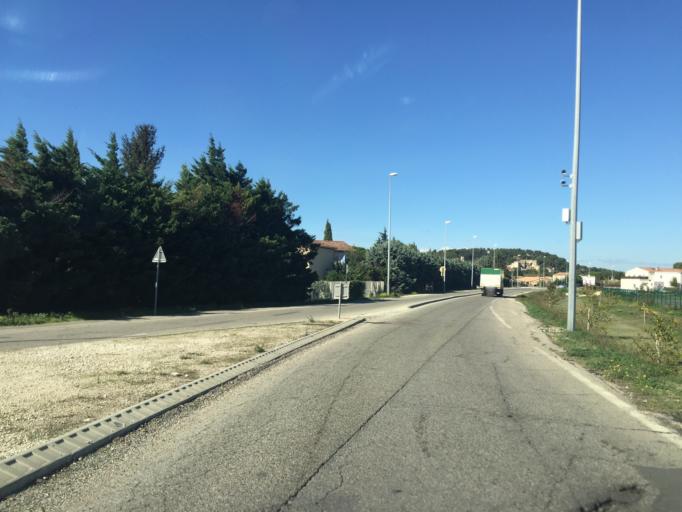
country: FR
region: Provence-Alpes-Cote d'Azur
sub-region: Departement du Vaucluse
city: Vedene
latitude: 43.9736
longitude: 4.9123
